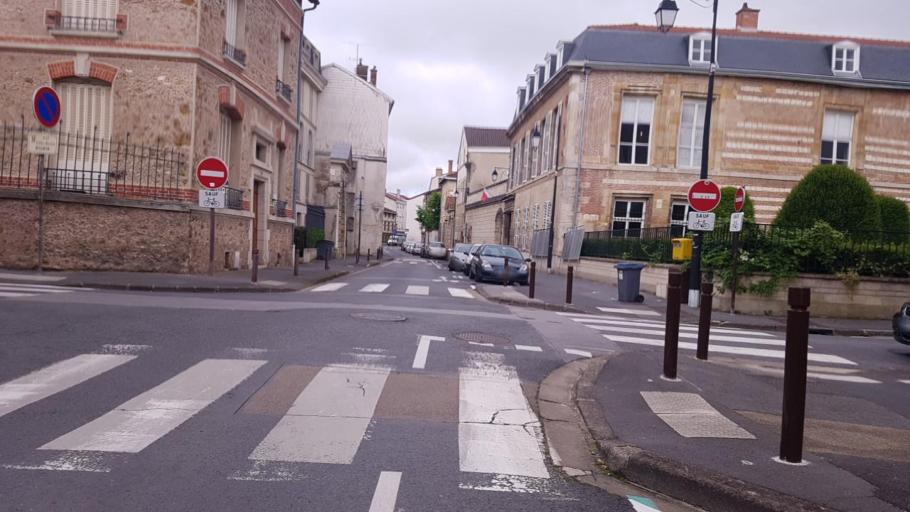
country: FR
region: Champagne-Ardenne
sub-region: Departement de la Marne
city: Chalons-en-Champagne
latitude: 48.9562
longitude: 4.3672
